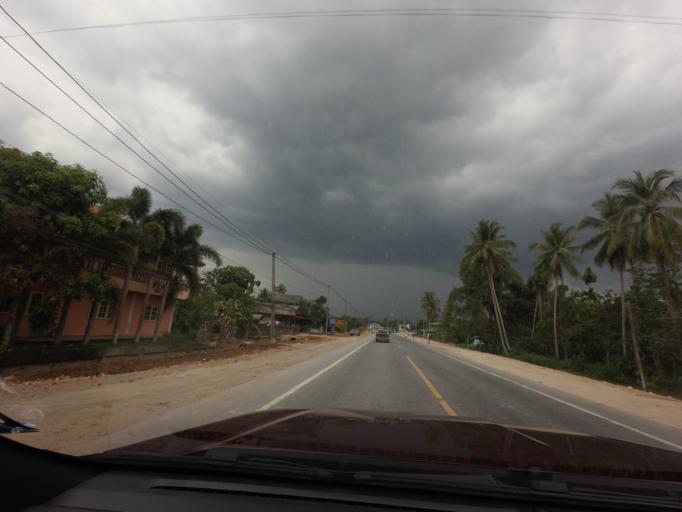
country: TH
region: Yala
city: Krong Pi Nang
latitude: 6.4286
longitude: 101.2781
